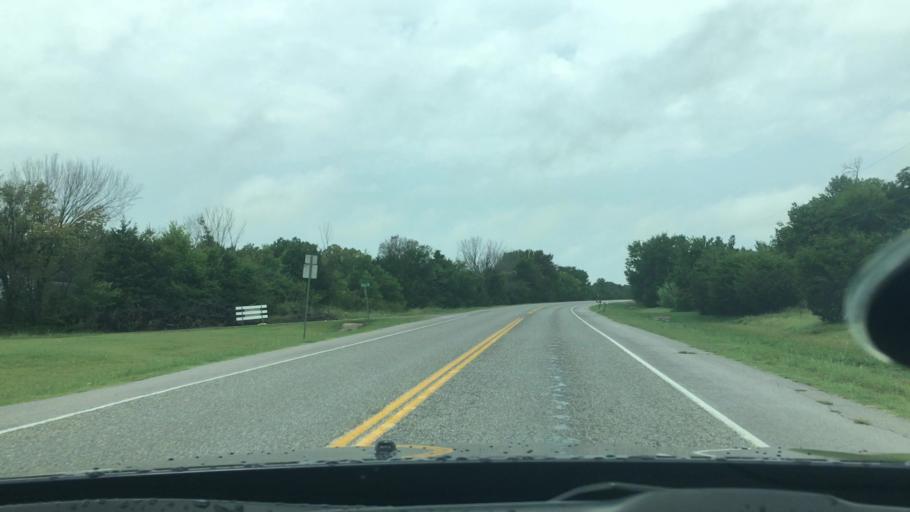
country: US
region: Oklahoma
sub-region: Johnston County
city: Tishomingo
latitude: 34.2476
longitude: -96.7568
